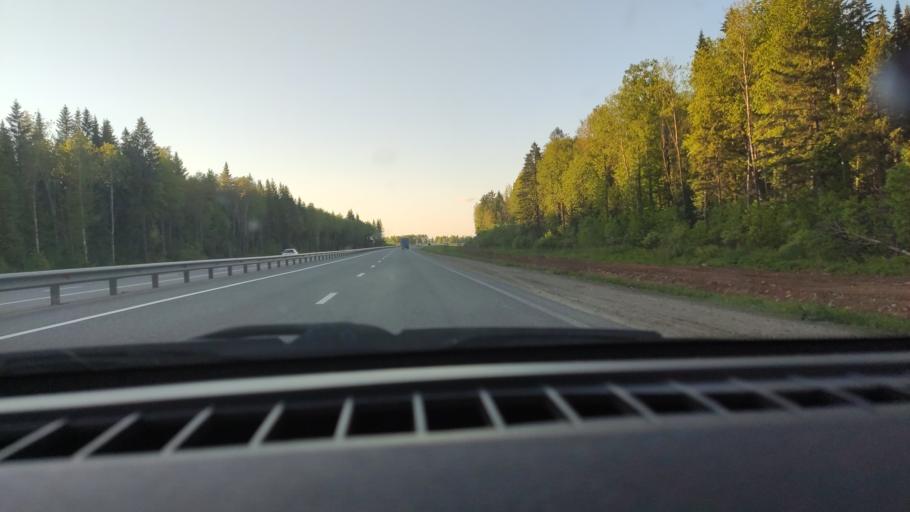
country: RU
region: Perm
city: Polazna
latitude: 58.2624
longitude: 56.4104
